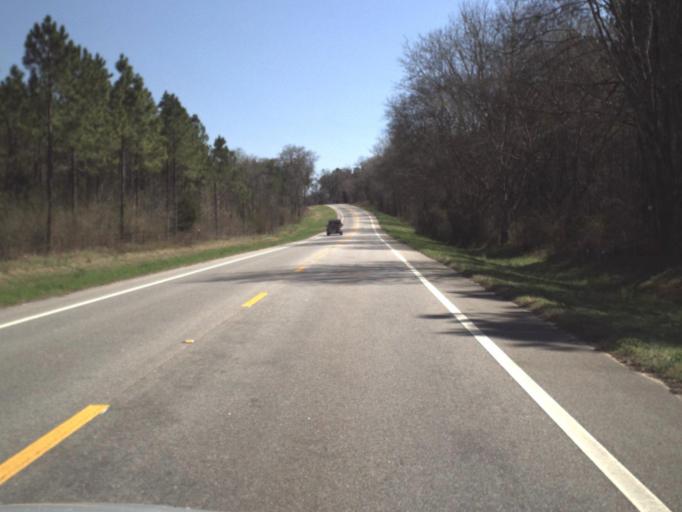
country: US
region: Florida
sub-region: Jackson County
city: Marianna
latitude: 30.8261
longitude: -85.3302
